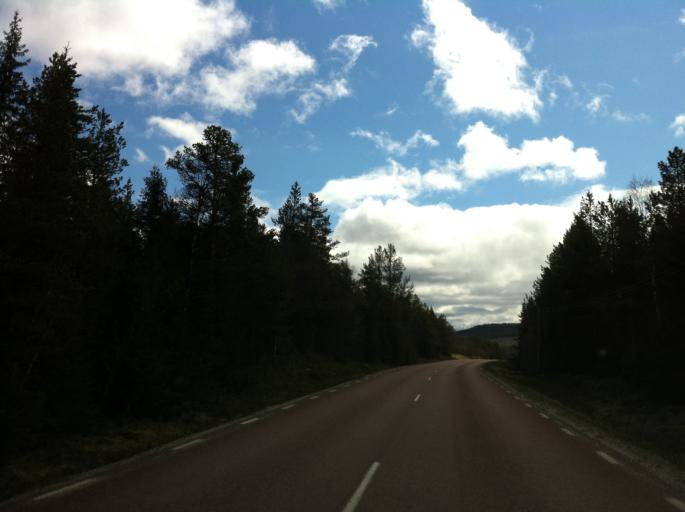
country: SE
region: Jaemtland
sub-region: Are Kommun
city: Are
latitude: 62.5623
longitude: 12.5652
